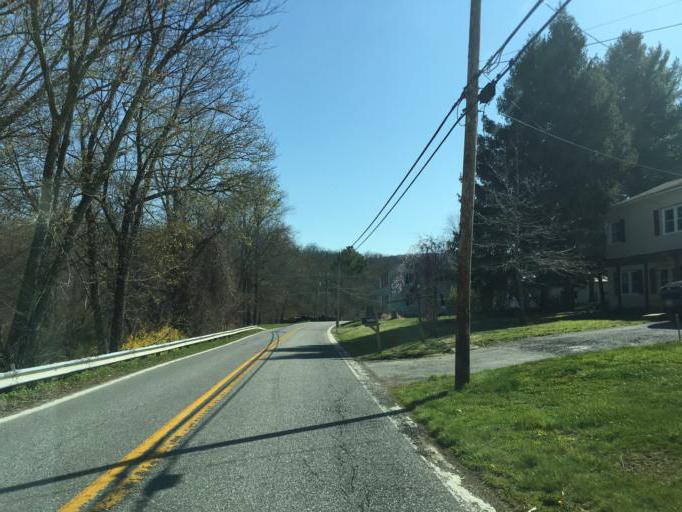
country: US
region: Maryland
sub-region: Frederick County
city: Myersville
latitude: 39.5731
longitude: -77.5469
